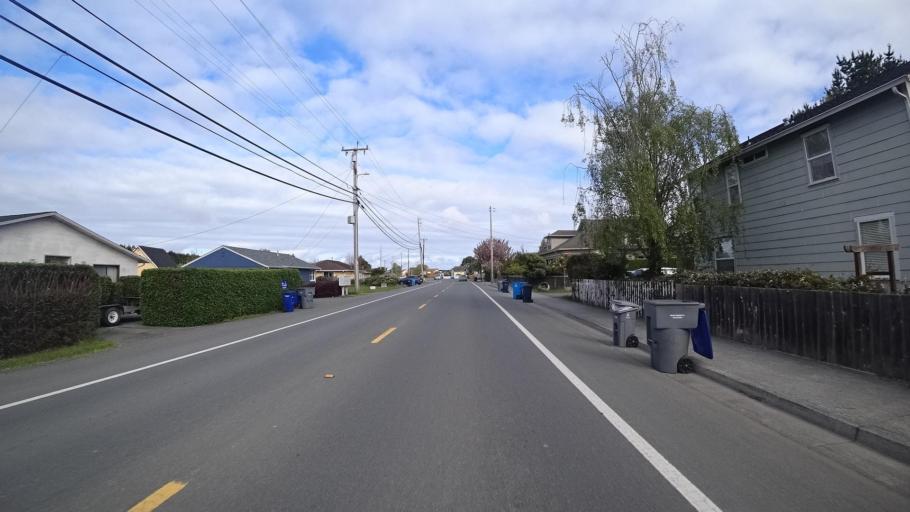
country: US
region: California
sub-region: Humboldt County
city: Arcata
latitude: 40.8919
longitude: -124.0911
